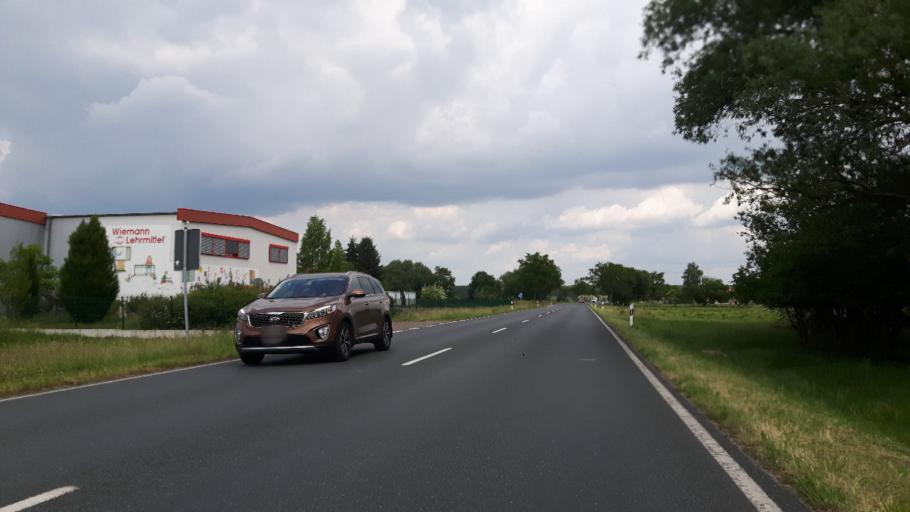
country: DE
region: Saxony-Anhalt
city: Schlaitz
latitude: 51.6598
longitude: 12.4371
